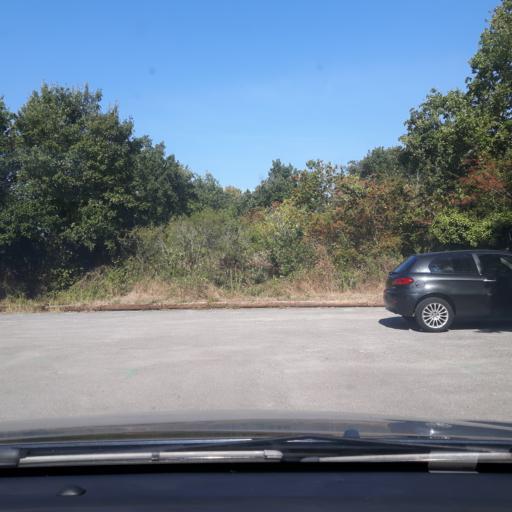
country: FR
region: Midi-Pyrenees
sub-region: Departement de la Haute-Garonne
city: Paulhac
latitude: 43.7789
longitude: 1.5667
